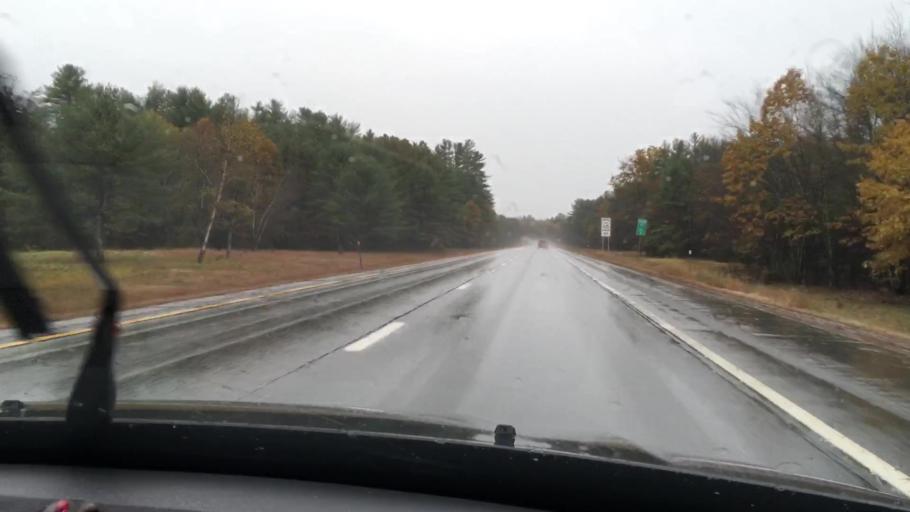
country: US
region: New Hampshire
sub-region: Merrimack County
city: East Concord
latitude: 43.2818
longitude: -71.5673
